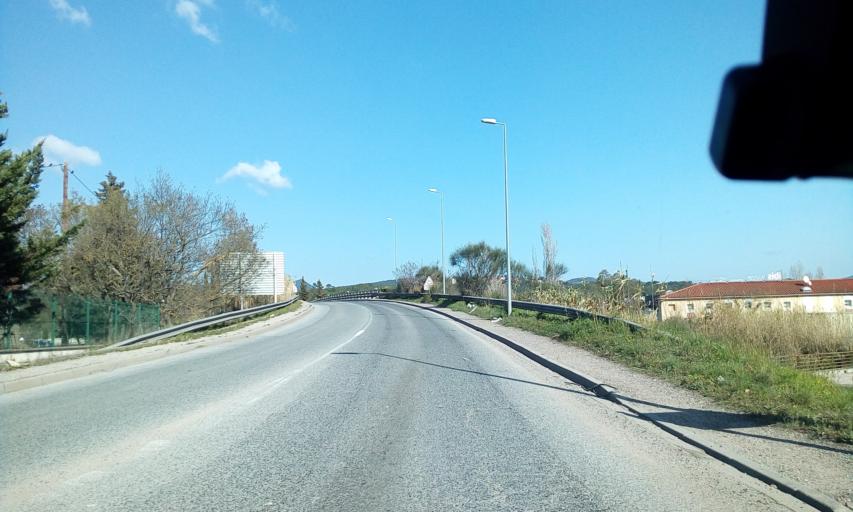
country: FR
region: Provence-Alpes-Cote d'Azur
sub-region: Departement du Var
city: Frejus
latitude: 43.4686
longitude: 6.7331
